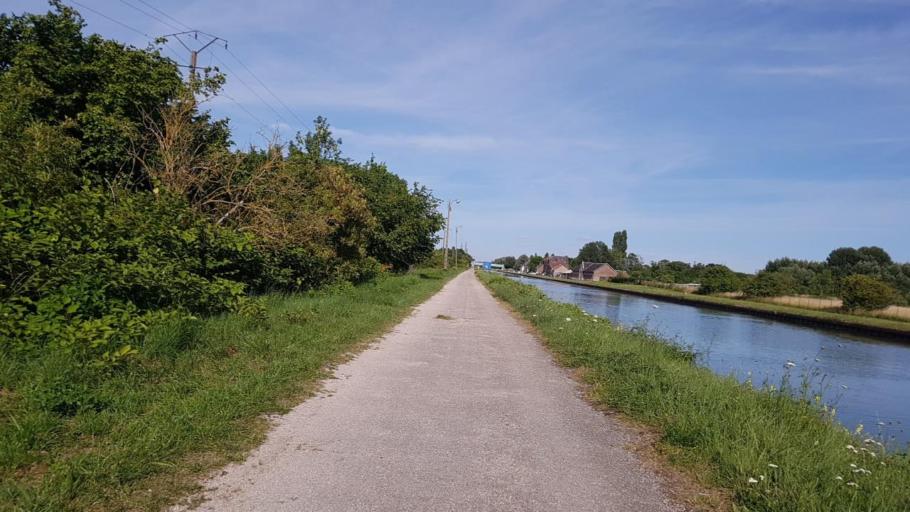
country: FR
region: Picardie
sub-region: Departement de l'Aisne
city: Tergnier
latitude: 49.6508
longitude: 3.3070
